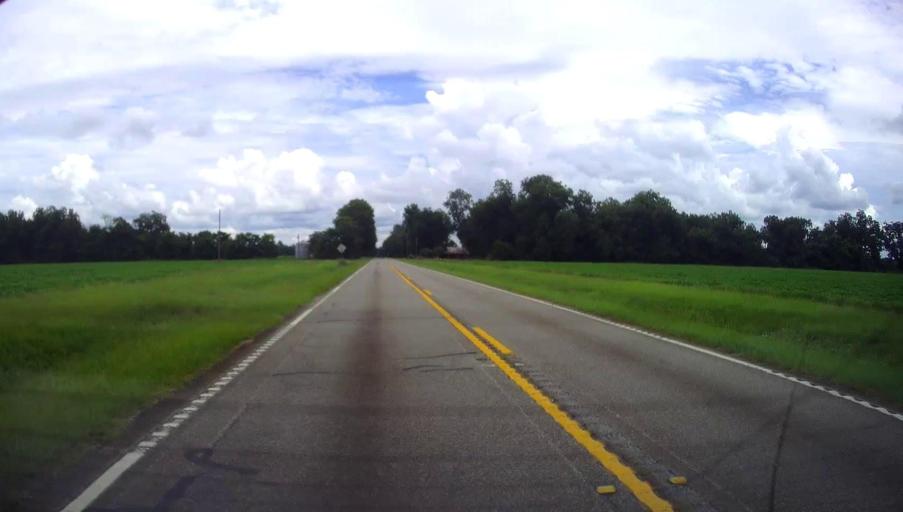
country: US
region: Georgia
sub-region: Schley County
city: Ellaville
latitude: 32.2249
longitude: -84.2819
